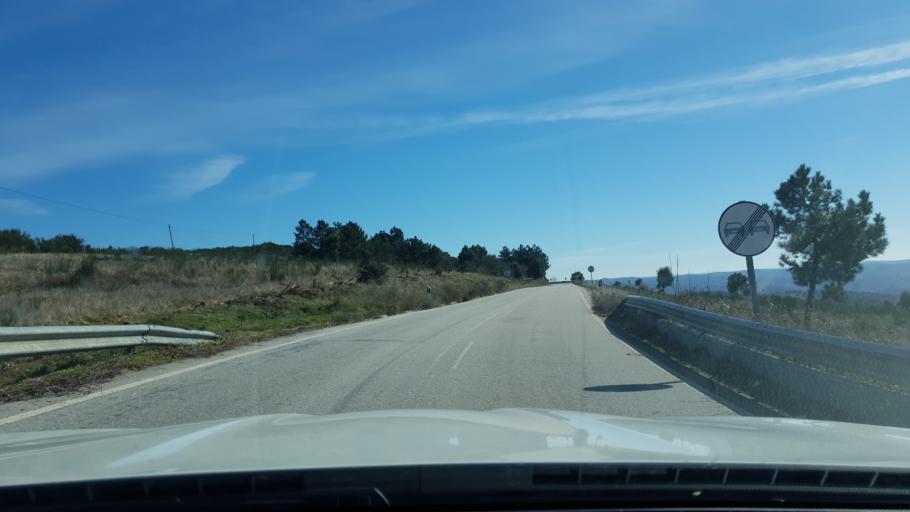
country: PT
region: Braganca
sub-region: Torre de Moncorvo
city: Torre de Moncorvo
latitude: 41.1803
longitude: -6.9310
